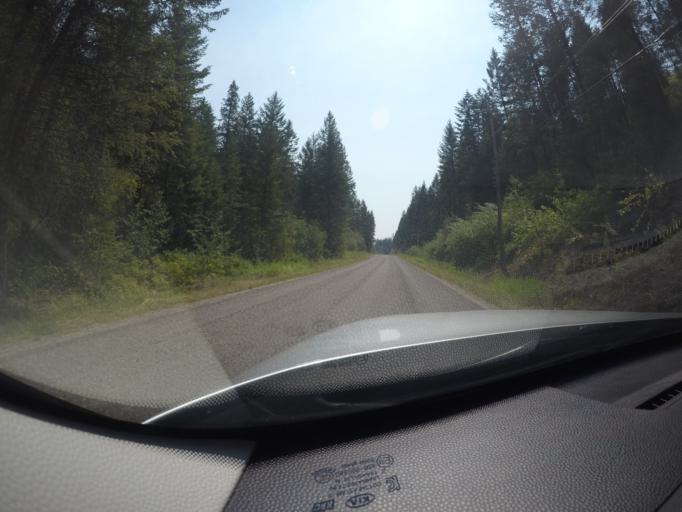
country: US
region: Montana
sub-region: Lake County
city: Polson
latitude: 47.7715
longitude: -114.1690
